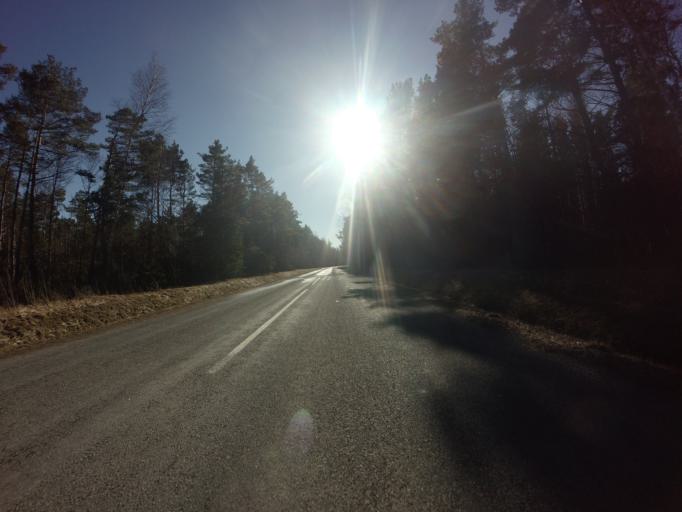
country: EE
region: Saare
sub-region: Kuressaare linn
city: Kuressaare
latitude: 58.4885
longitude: 22.3015
